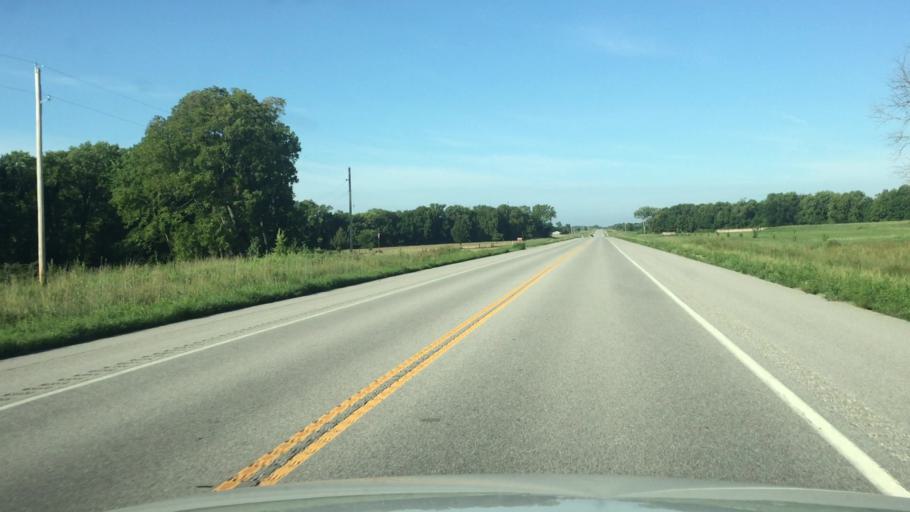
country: US
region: Kansas
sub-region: Miami County
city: Osawatomie
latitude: 38.4231
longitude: -95.0283
